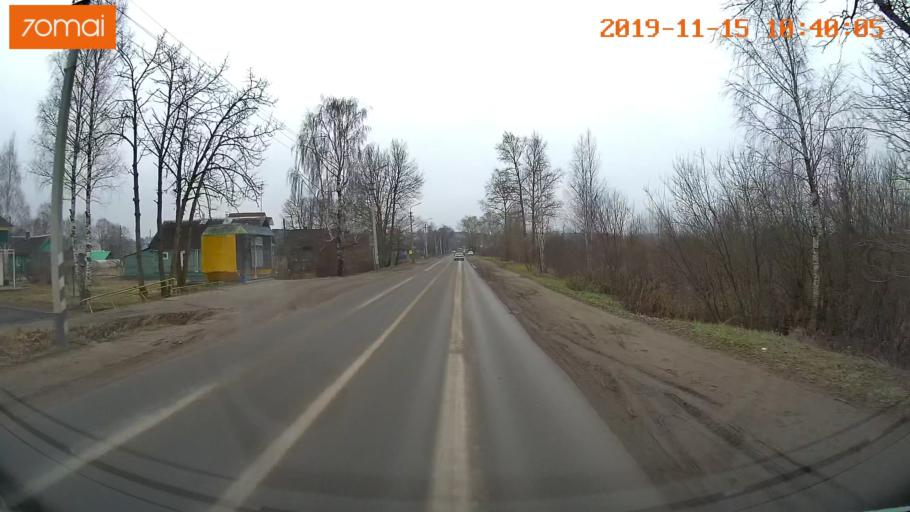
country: RU
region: Vologda
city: Sheksna
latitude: 59.2168
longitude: 38.5102
